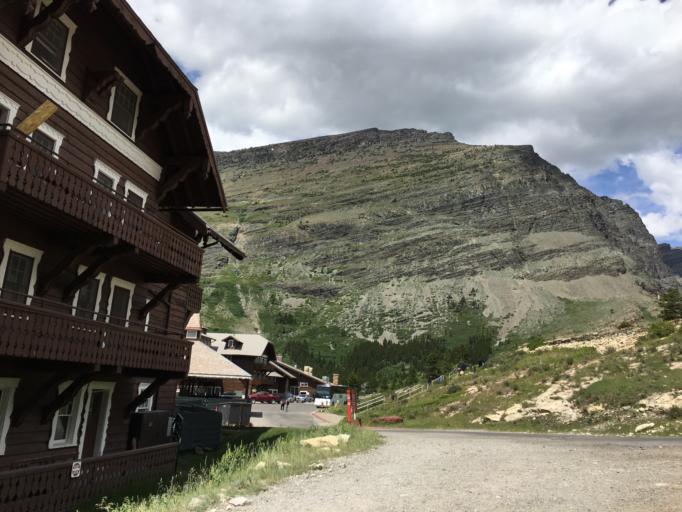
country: CA
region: Alberta
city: Cardston
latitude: 48.7959
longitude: -113.6573
